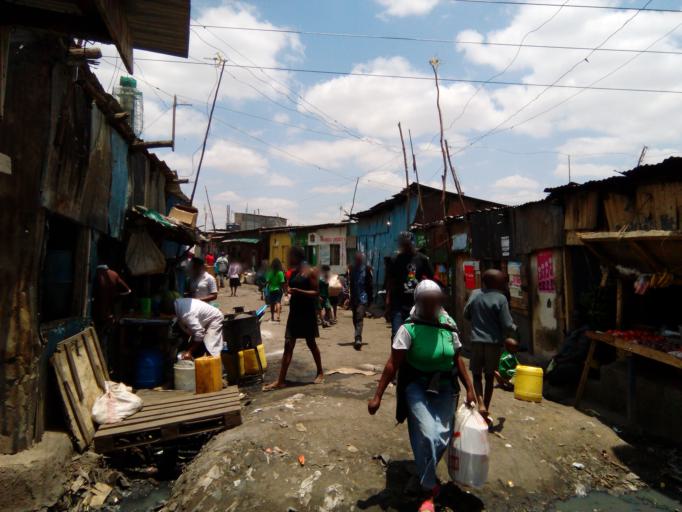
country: KE
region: Nairobi Area
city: Pumwani
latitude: -1.3082
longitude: 36.8392
